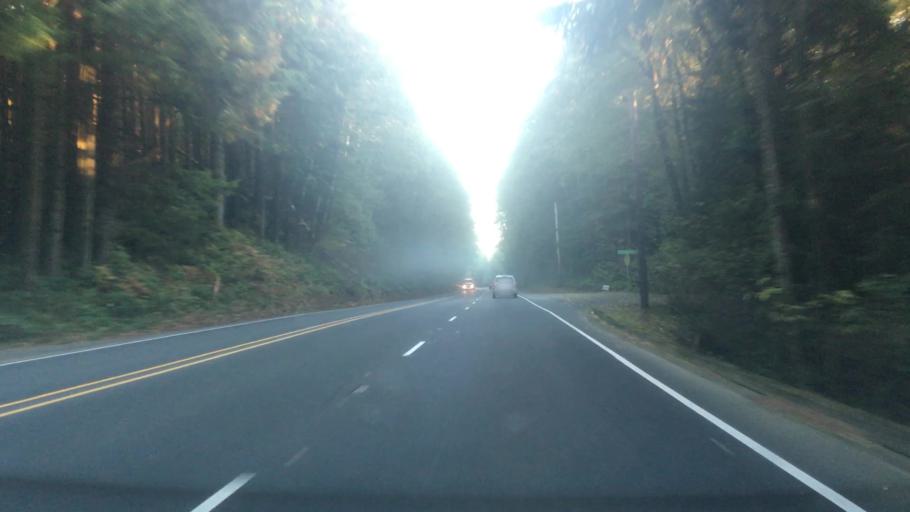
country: US
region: Oregon
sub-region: Clatsop County
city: Cannon Beach
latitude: 45.7922
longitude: -123.9608
